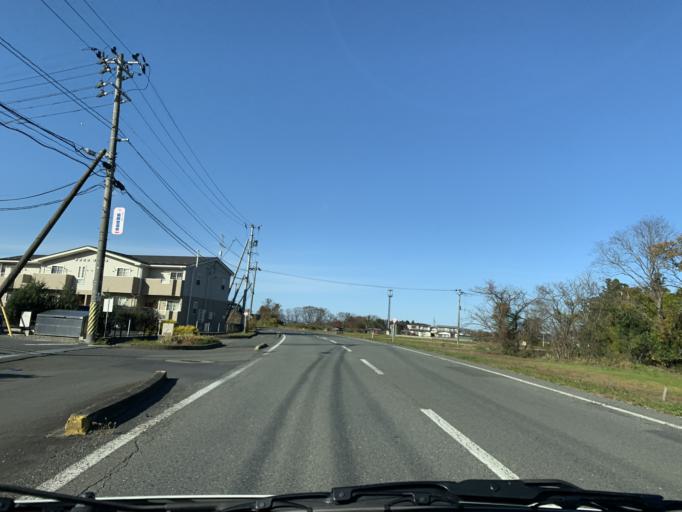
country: JP
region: Iwate
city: Mizusawa
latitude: 39.1729
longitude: 141.1407
